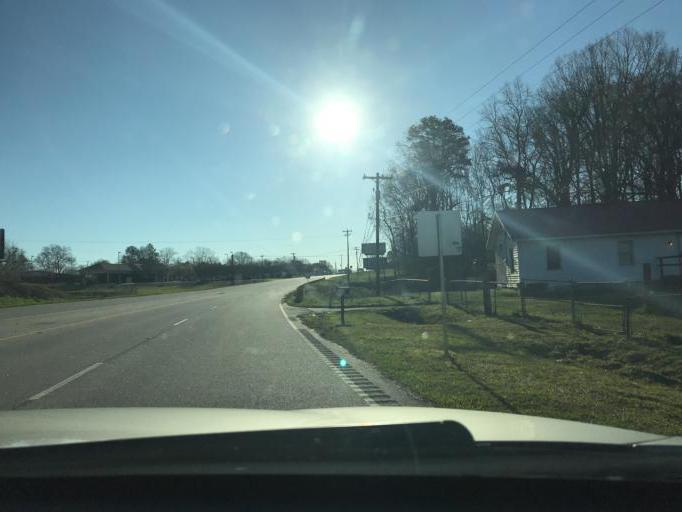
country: US
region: South Carolina
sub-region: Laurens County
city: Clinton
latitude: 34.4719
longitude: -81.9149
